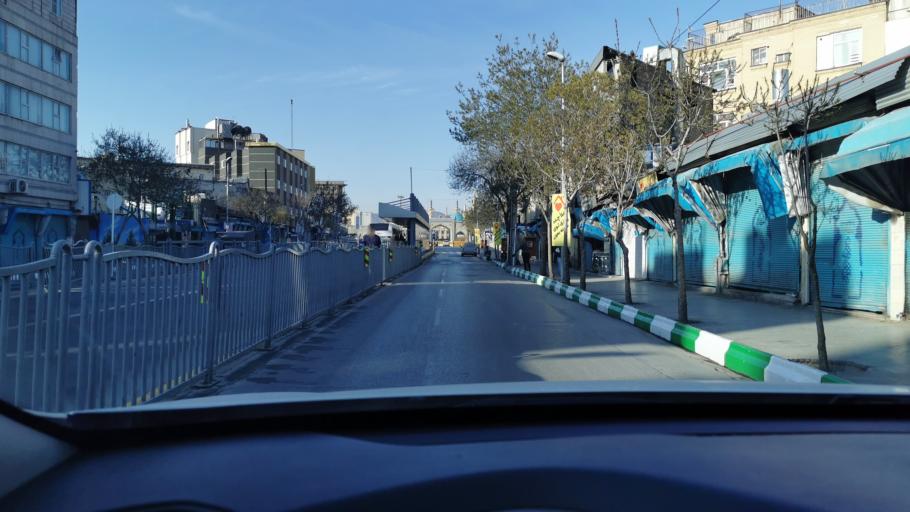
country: IR
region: Razavi Khorasan
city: Mashhad
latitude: 36.2915
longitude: 59.6213
